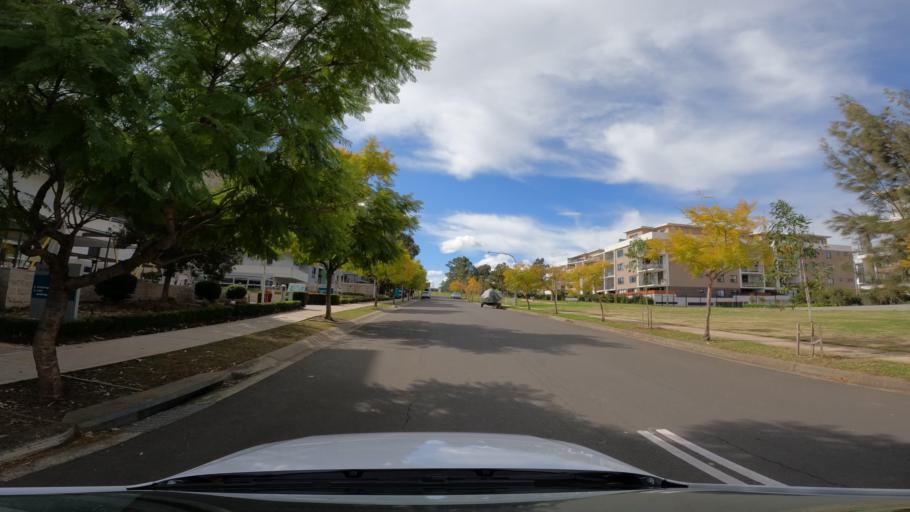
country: AU
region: New South Wales
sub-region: Blacktown
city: Stanhope Gardens
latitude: -33.7214
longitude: 150.9439
